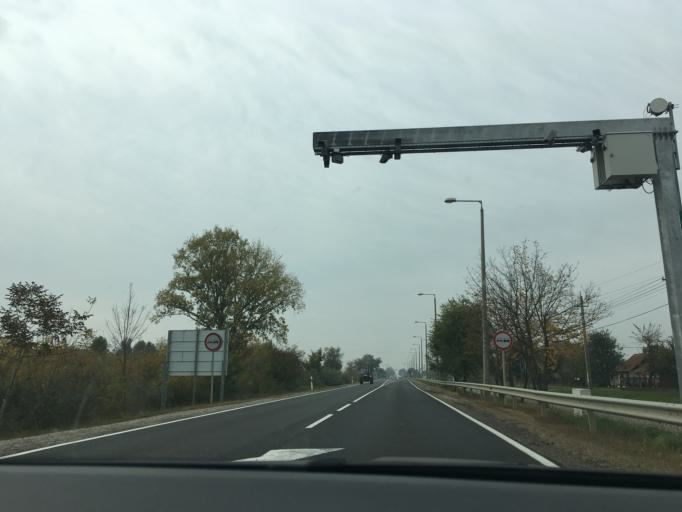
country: HU
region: Hajdu-Bihar
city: Puspokladany
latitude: 47.3322
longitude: 21.1277
